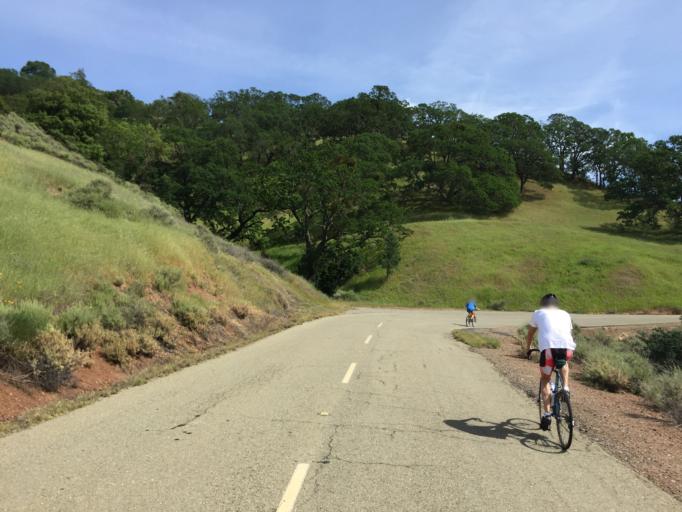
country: US
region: California
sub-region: Contra Costa County
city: Diablo
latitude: 37.8819
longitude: -121.9692
